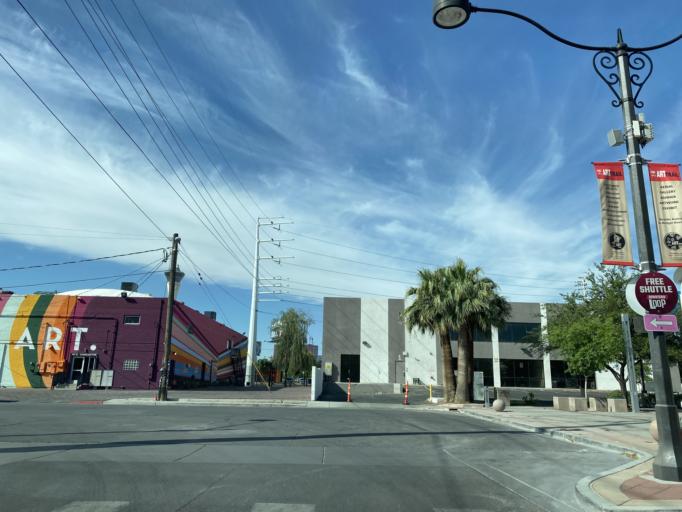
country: US
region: Nevada
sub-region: Clark County
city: Las Vegas
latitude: 36.1598
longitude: -115.1528
